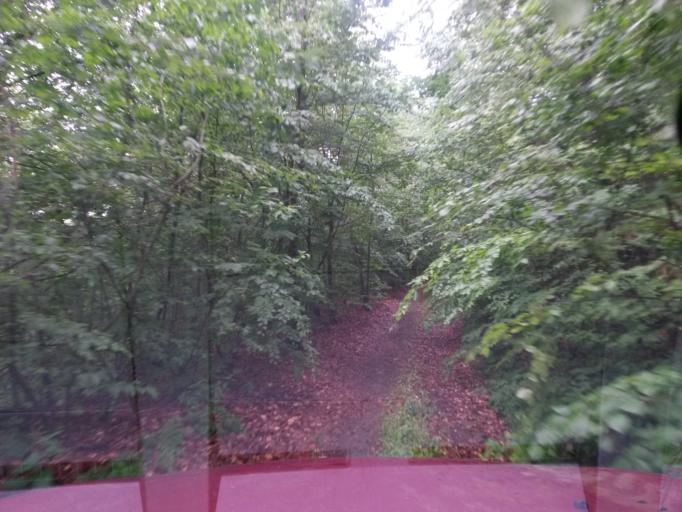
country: SK
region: Kosicky
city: Kosice
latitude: 48.7233
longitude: 21.1533
